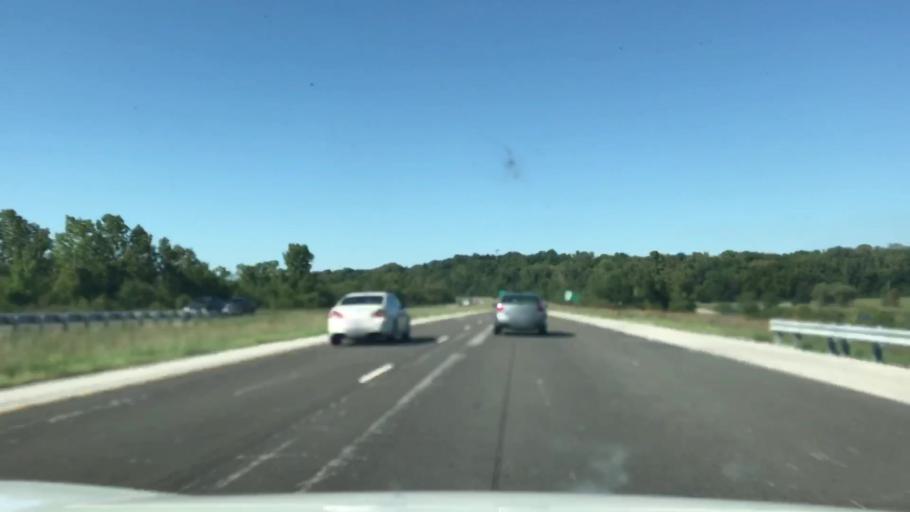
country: US
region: Illinois
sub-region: Madison County
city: South Roxana
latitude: 38.8341
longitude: -90.0435
